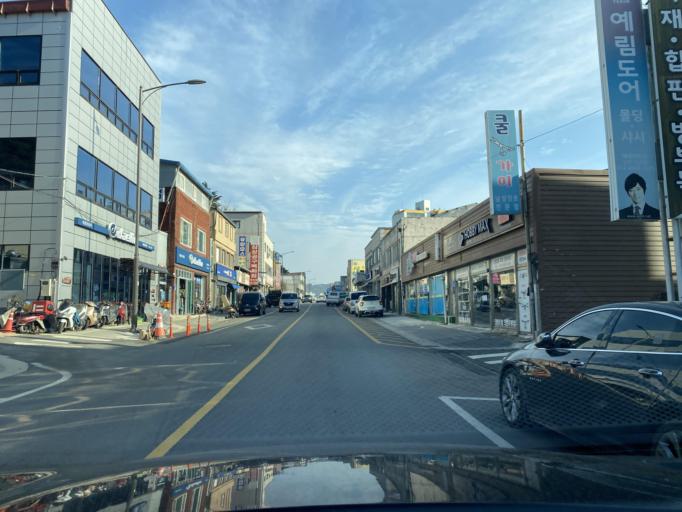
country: KR
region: Chungcheongnam-do
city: Yesan
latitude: 36.6802
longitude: 126.8354
